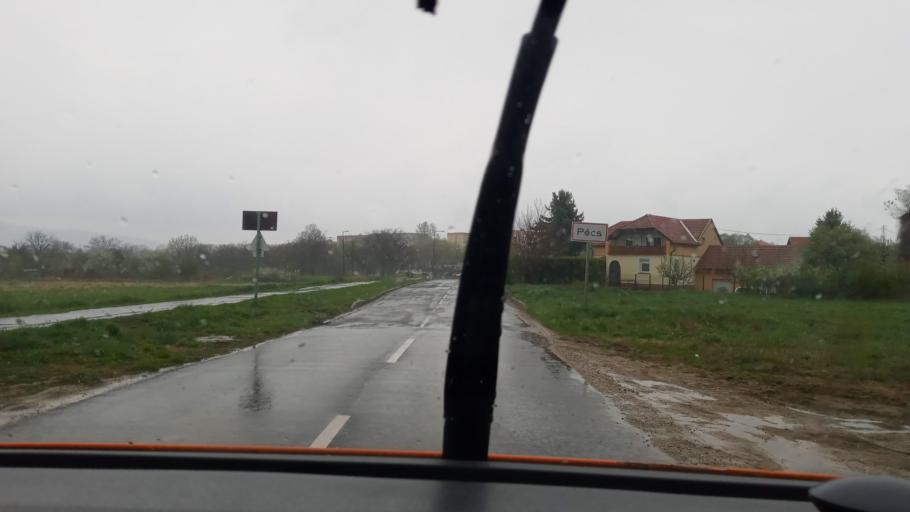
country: HU
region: Baranya
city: Pellerd
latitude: 46.0287
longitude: 18.2102
